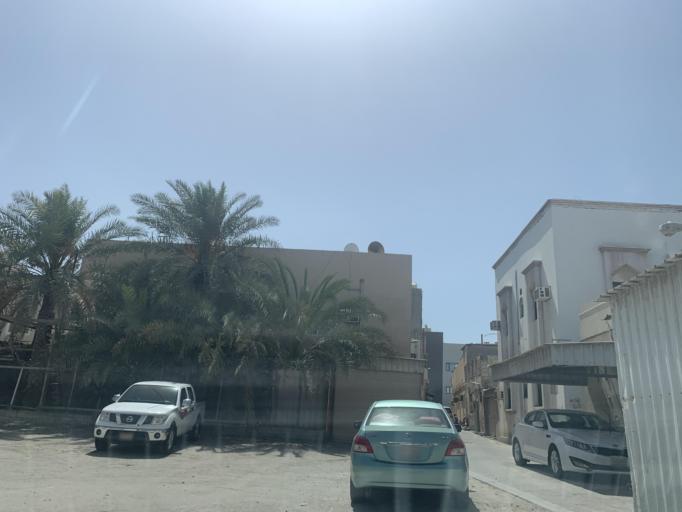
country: BH
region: Northern
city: Sitrah
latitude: 26.1616
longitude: 50.6084
